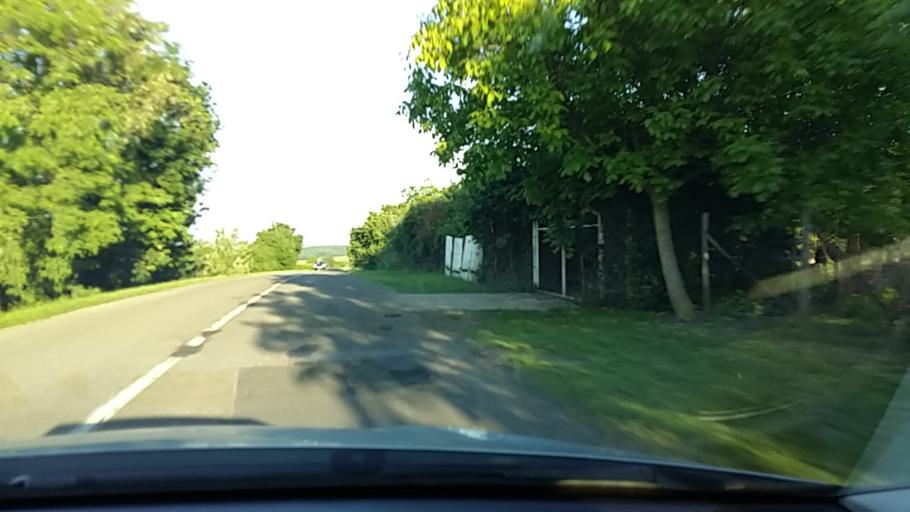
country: HU
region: Nograd
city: Diosjeno
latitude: 47.9049
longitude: 19.0687
